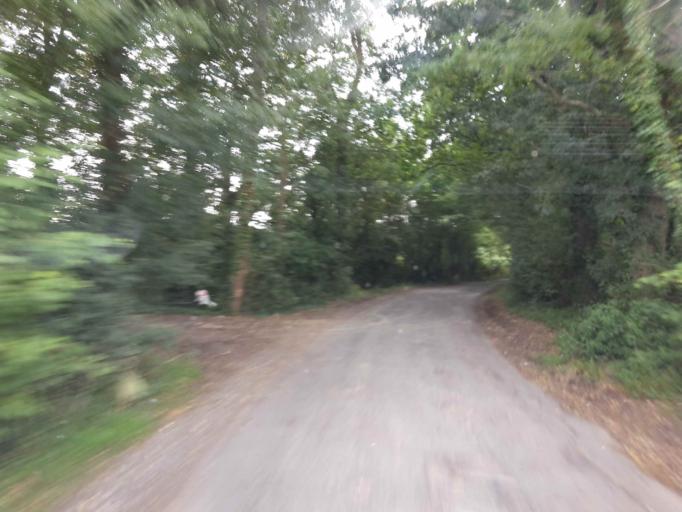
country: GB
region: England
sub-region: West Sussex
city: Billingshurst
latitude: 51.0248
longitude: -0.4344
